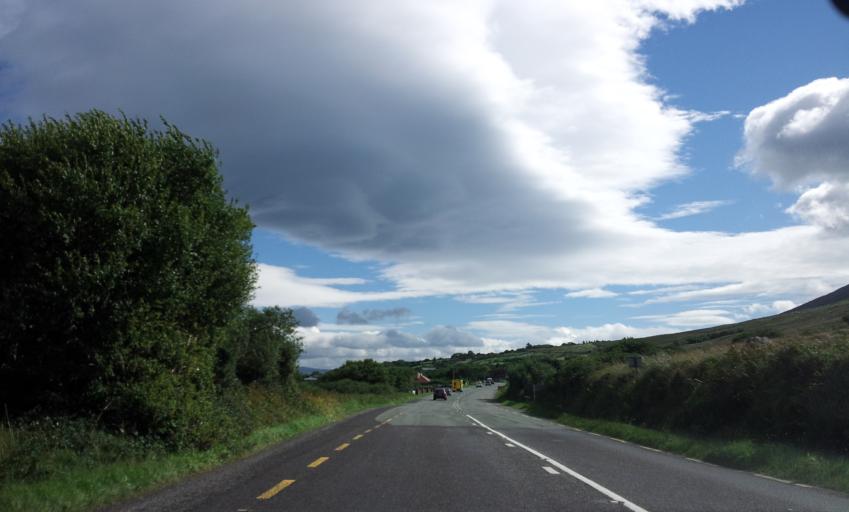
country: IE
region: Munster
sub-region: Ciarrai
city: Killorglin
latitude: 52.2330
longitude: -9.8601
